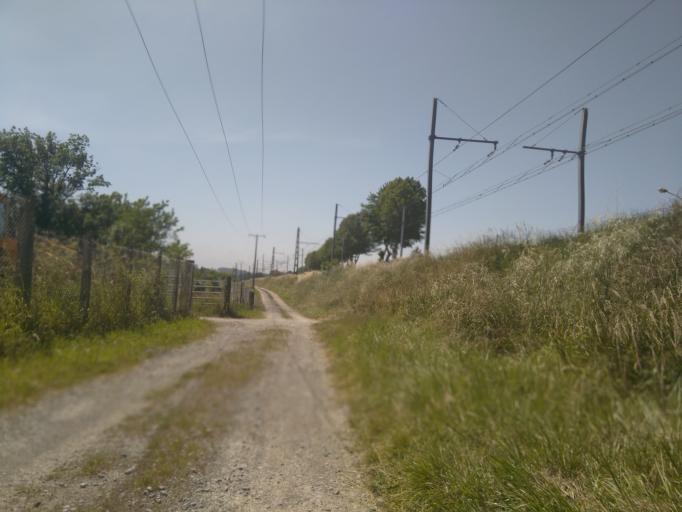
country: FR
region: Aquitaine
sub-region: Departement des Pyrenees-Atlantiques
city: Orthez
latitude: 43.4896
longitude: -0.7893
